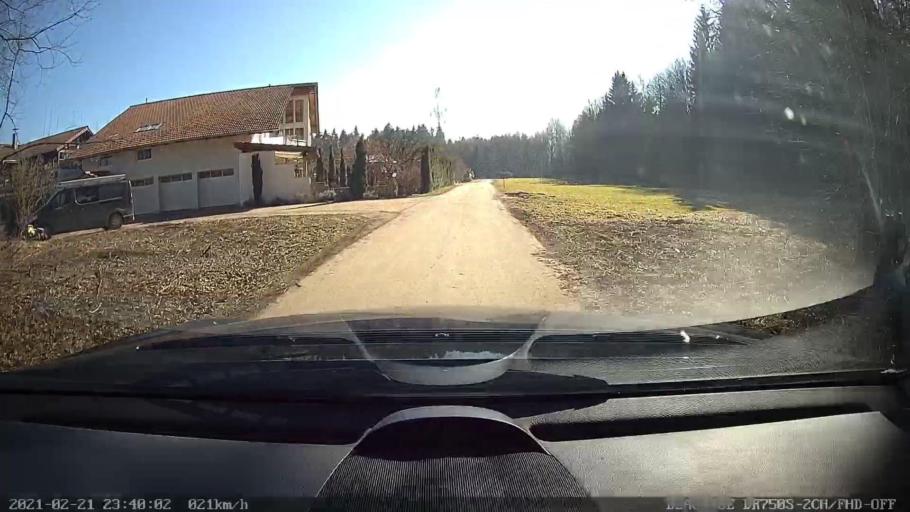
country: DE
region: Bavaria
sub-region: Upper Bavaria
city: Schonstett
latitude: 47.9918
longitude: 12.2172
